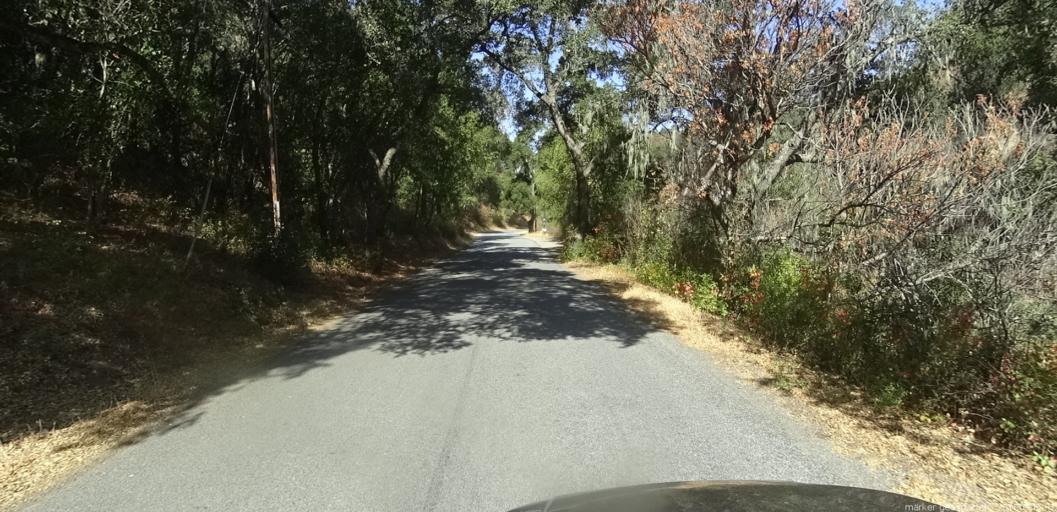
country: US
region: California
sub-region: Monterey County
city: Gonzales
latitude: 36.3911
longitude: -121.5993
